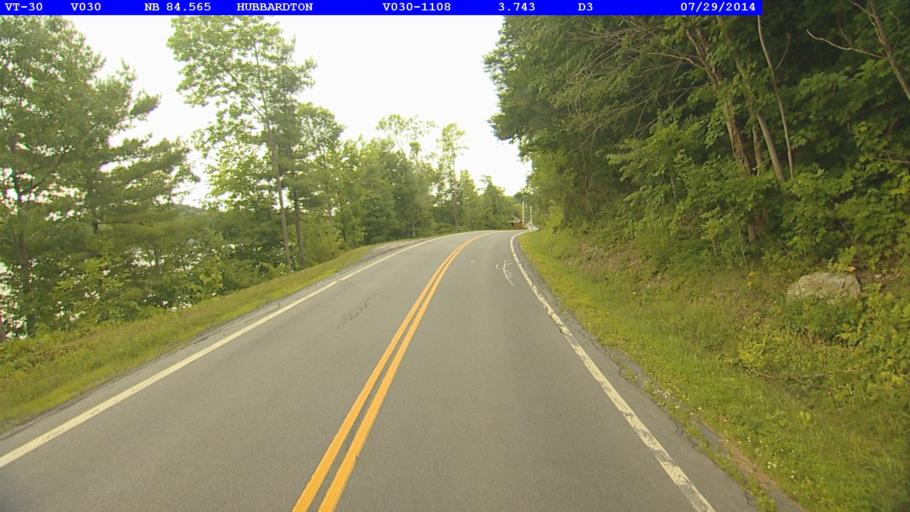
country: US
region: Vermont
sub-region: Rutland County
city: Brandon
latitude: 43.7314
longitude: -73.1805
